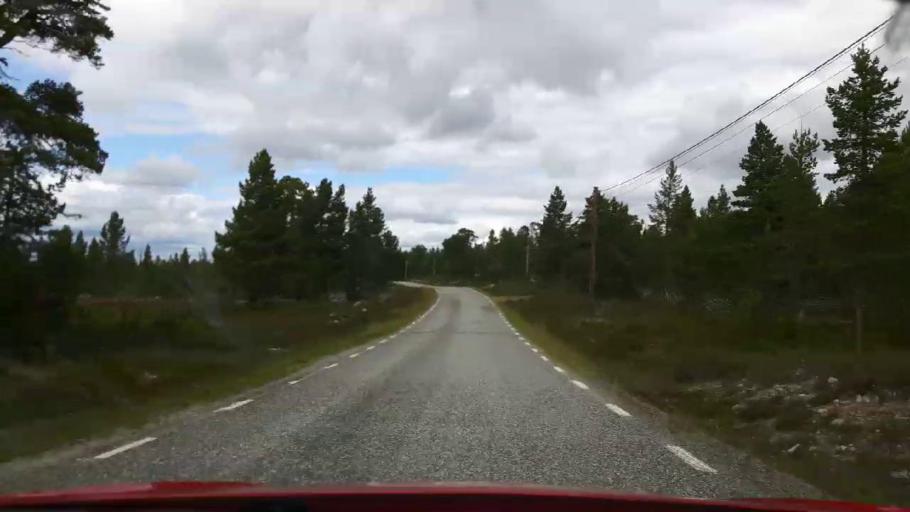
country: NO
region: Hedmark
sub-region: Engerdal
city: Engerdal
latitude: 62.3278
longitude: 12.8083
